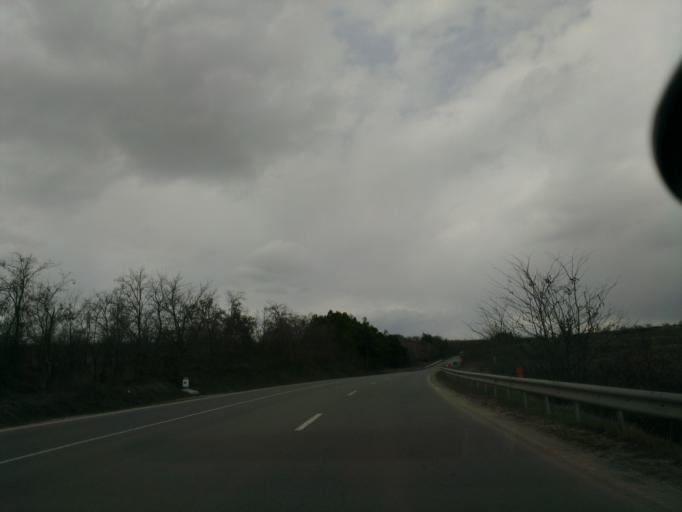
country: MD
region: Hincesti
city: Hincesti
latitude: 46.8747
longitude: 28.6484
